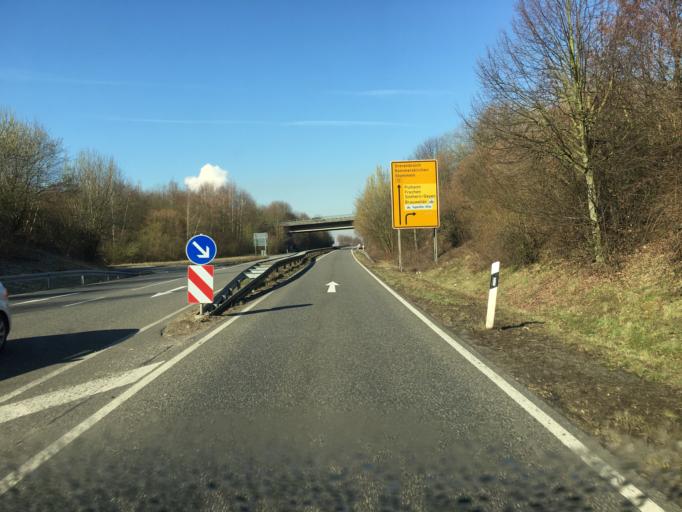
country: DE
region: North Rhine-Westphalia
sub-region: Regierungsbezirk Koln
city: Pulheim
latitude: 50.9861
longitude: 6.8017
